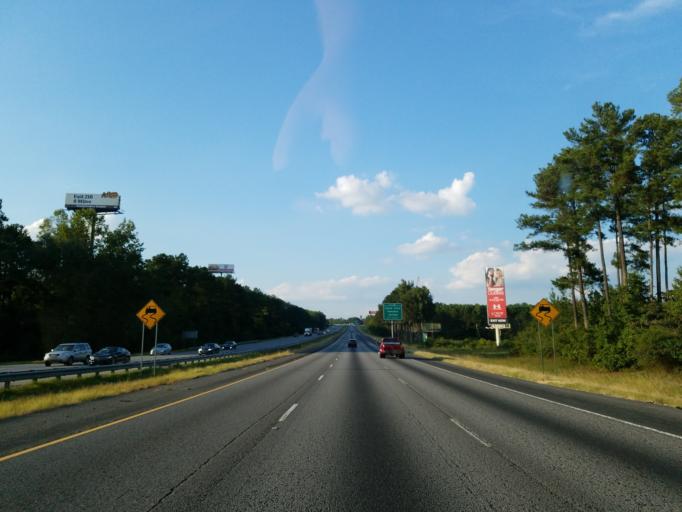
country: US
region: Georgia
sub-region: Henry County
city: Locust Grove
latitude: 33.3405
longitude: -84.1231
